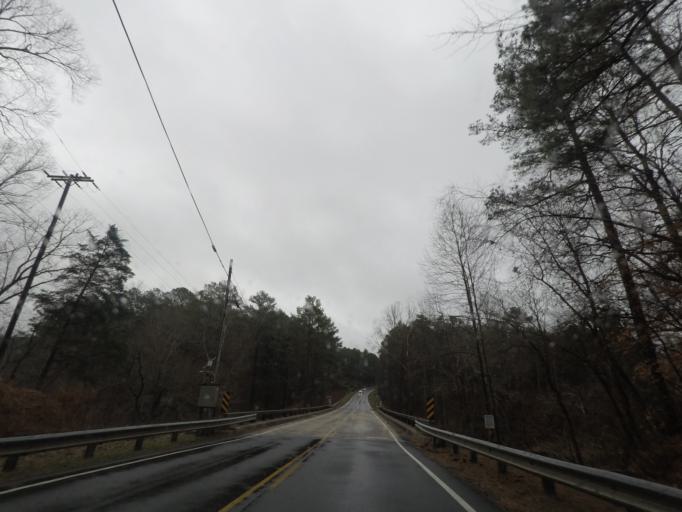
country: US
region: North Carolina
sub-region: Durham County
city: Durham
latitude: 36.0590
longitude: -78.9793
